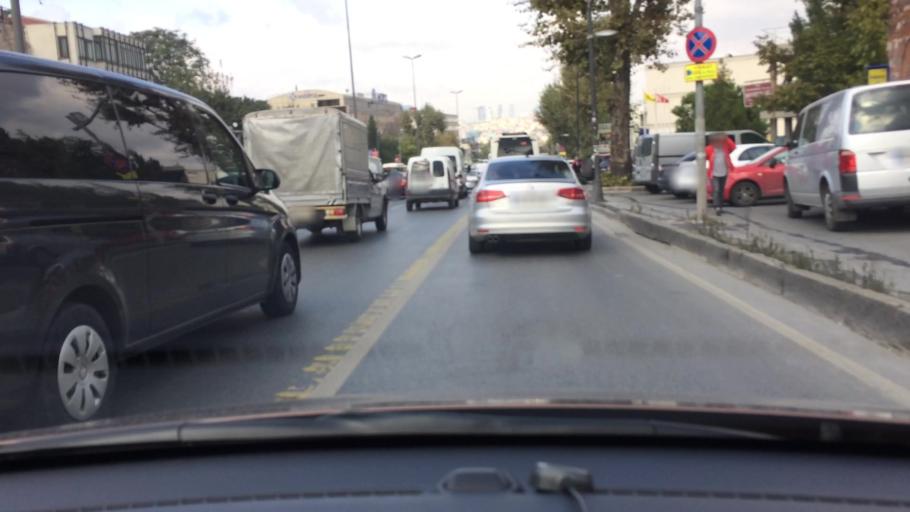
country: TR
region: Istanbul
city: Istanbul
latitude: 41.0195
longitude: 28.9587
